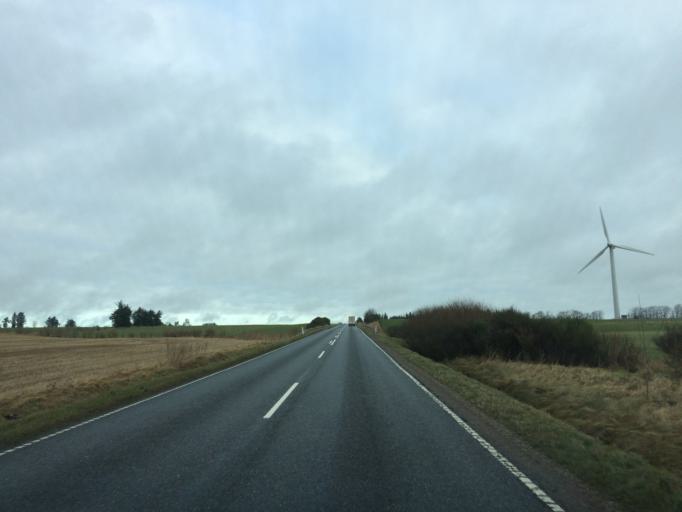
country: DK
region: Central Jutland
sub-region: Struer Kommune
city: Struer
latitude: 56.4231
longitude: 8.5038
